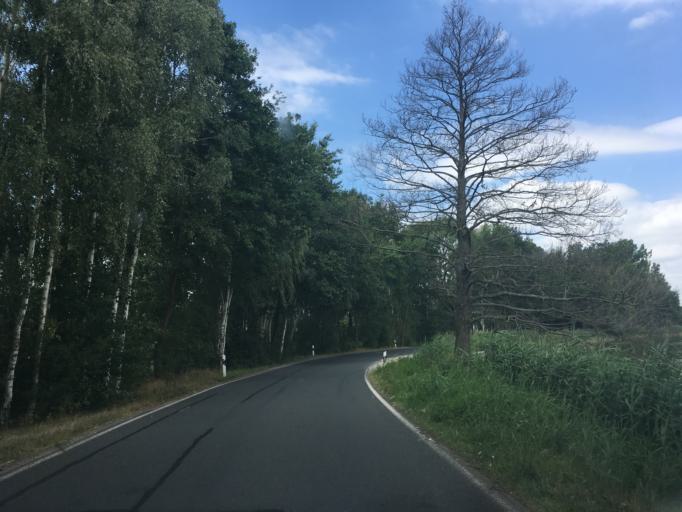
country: DE
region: Saxony
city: Tauscha
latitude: 51.2383
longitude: 13.7892
